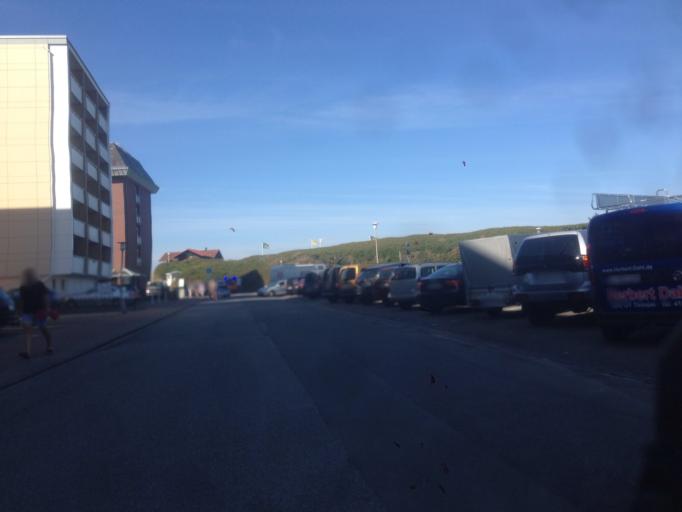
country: DE
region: Schleswig-Holstein
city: Westerland
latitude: 54.9118
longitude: 8.3028
